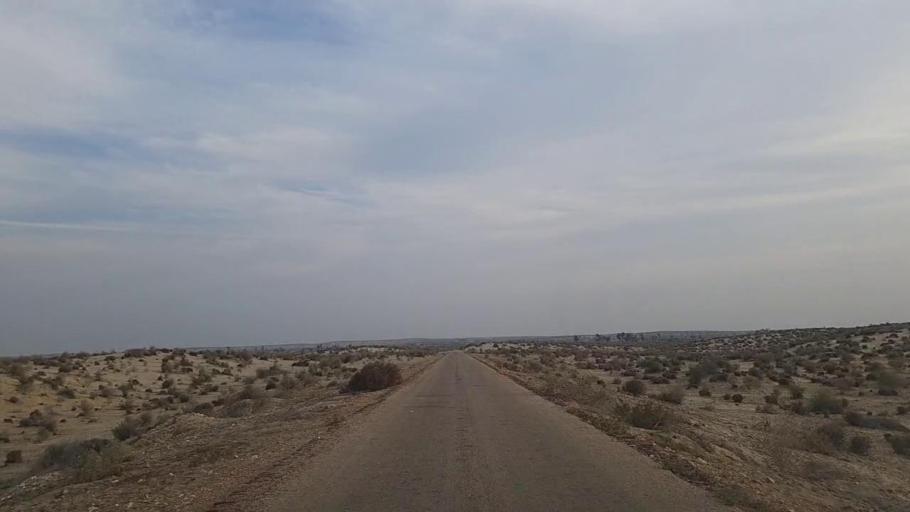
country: PK
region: Sindh
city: Daur
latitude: 26.5023
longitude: 68.5196
